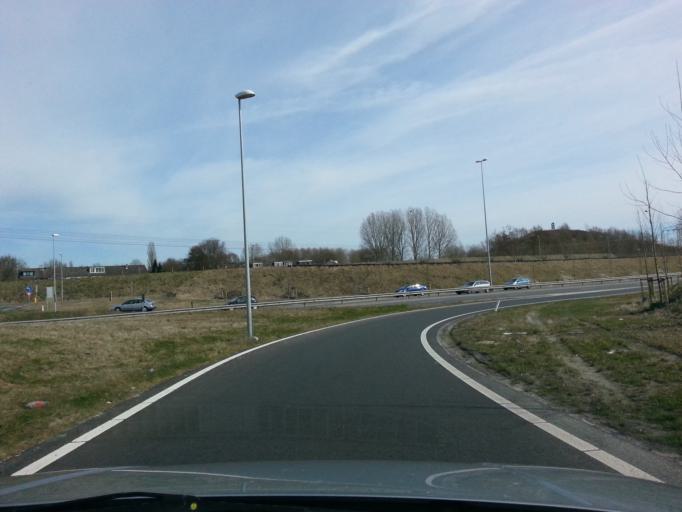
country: NL
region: Groningen
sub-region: Gemeente Groningen
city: Oosterpark
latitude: 53.2408
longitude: 6.5855
